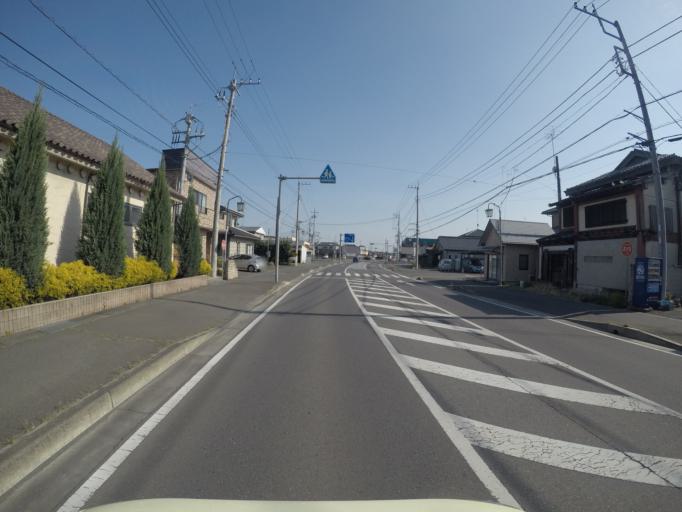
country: JP
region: Ibaraki
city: Yuki
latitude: 36.2957
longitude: 139.8771
